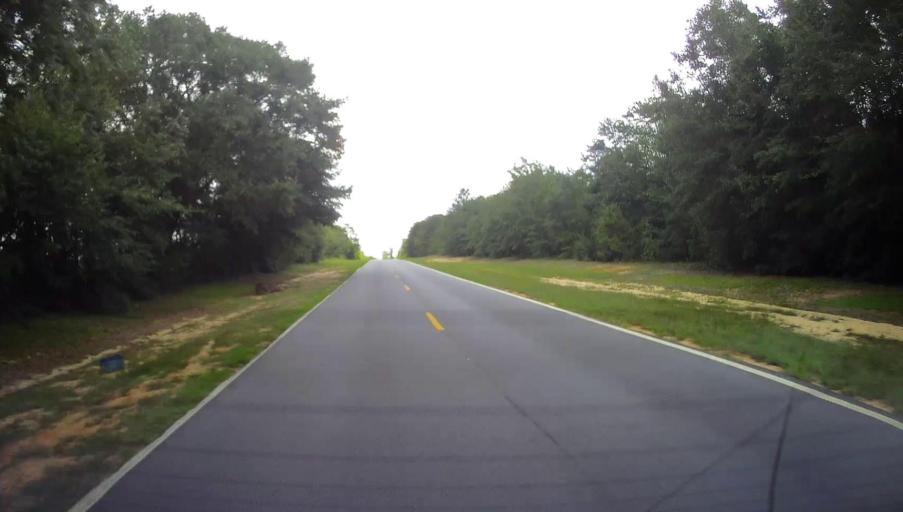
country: US
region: Georgia
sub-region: Chattahoochee County
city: Cusseta
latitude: 32.3100
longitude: -84.7417
